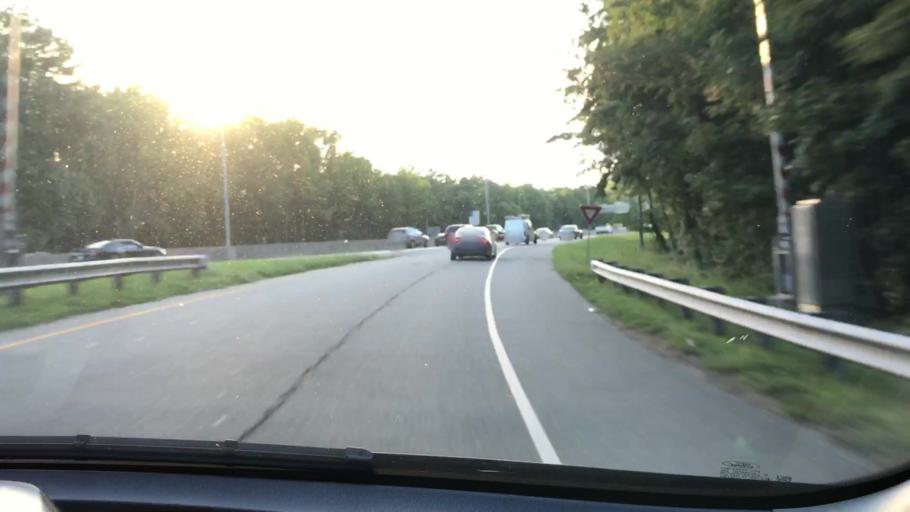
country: US
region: Virginia
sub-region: City of Hampton
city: Hampton
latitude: 37.0582
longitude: -76.4199
